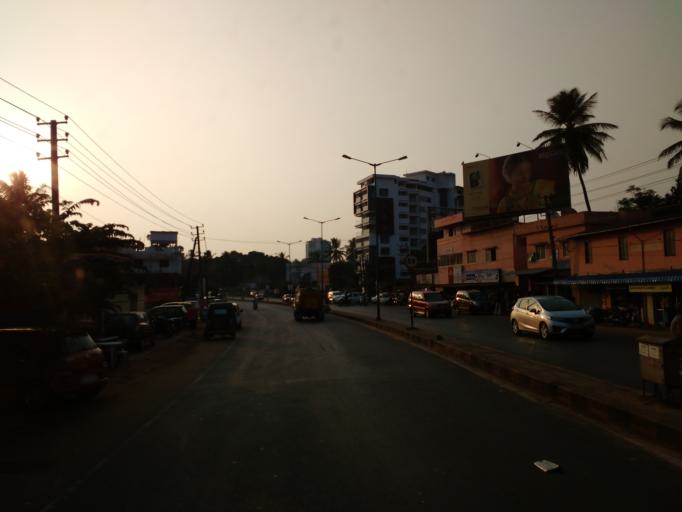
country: IN
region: Karnataka
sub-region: Dakshina Kannada
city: Mangalore
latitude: 12.8848
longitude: 74.8673
